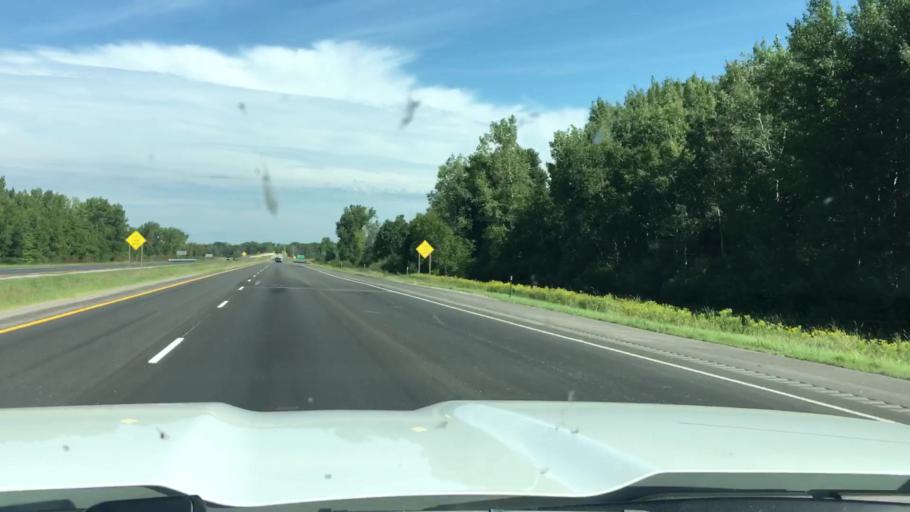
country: US
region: Michigan
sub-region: Saginaw County
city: Freeland
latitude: 43.5874
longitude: -84.1393
